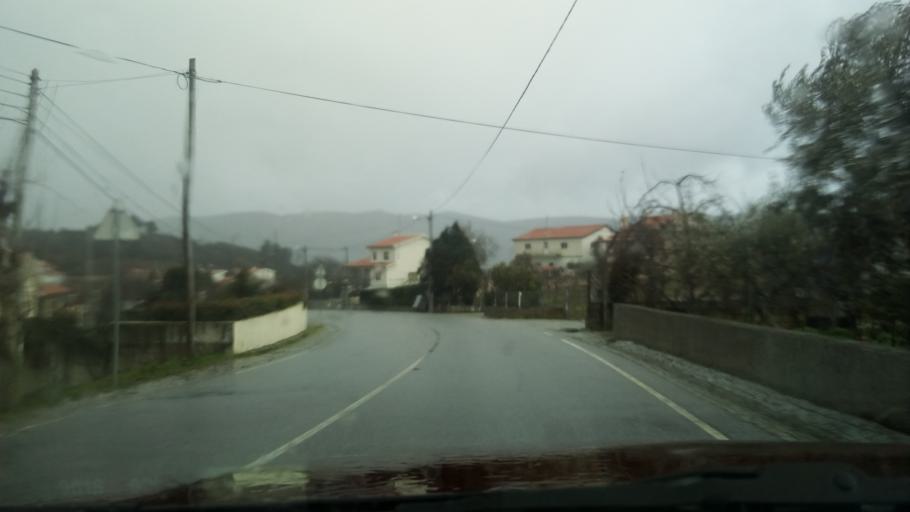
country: PT
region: Guarda
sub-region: Guarda
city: Guarda
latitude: 40.5433
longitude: -7.3230
